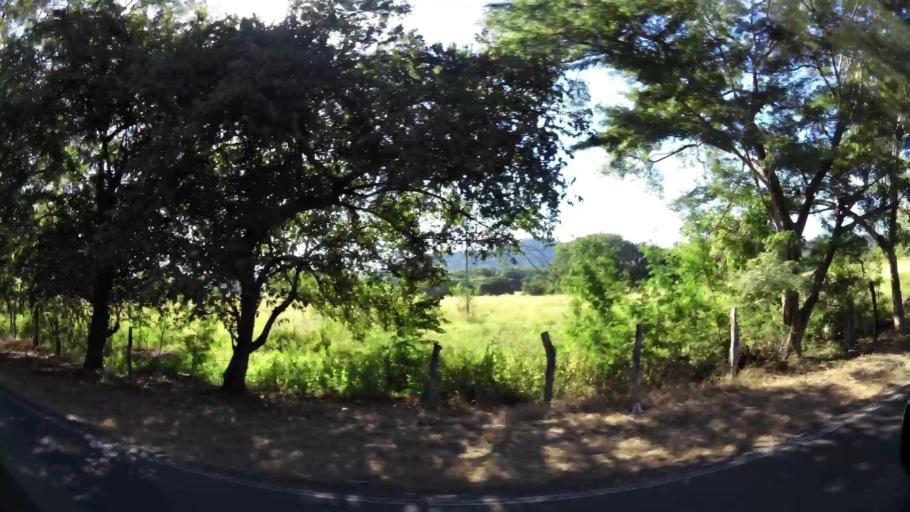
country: CR
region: Guanacaste
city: Belen
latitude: 10.3971
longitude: -85.6099
